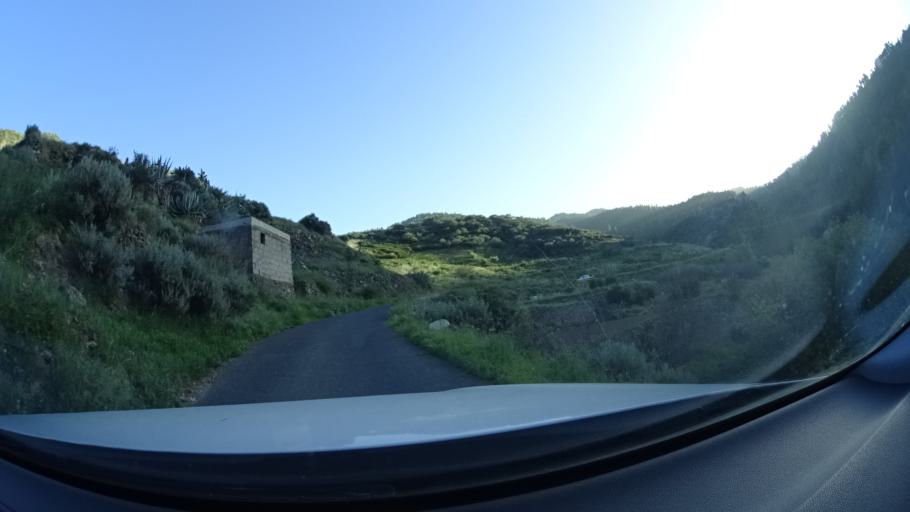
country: ES
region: Canary Islands
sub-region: Provincia de Las Palmas
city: Artenara
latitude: 28.0411
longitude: -15.6754
